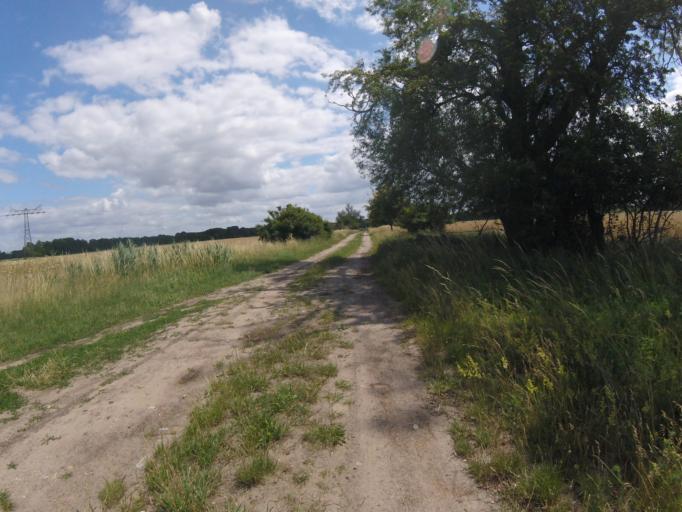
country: DE
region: Brandenburg
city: Mittenwalde
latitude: 52.2472
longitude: 13.5468
